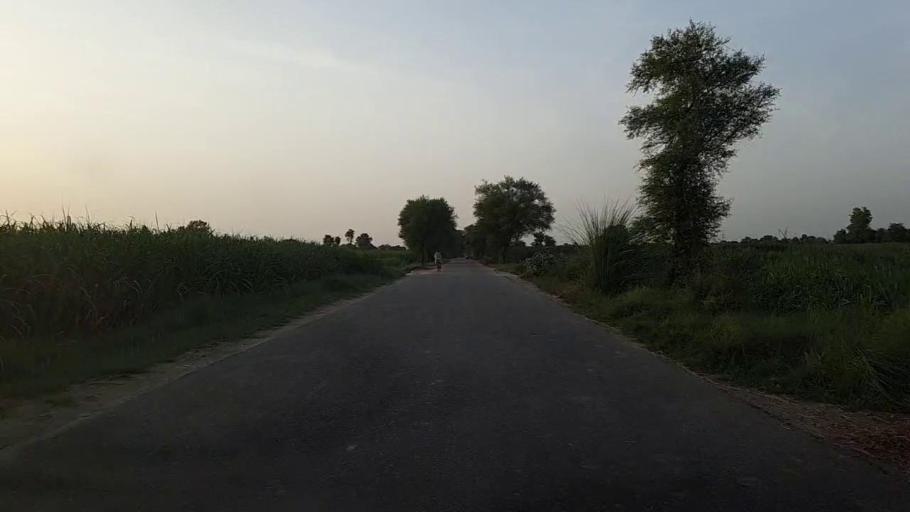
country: PK
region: Sindh
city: Ubauro
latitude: 28.2324
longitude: 69.8155
